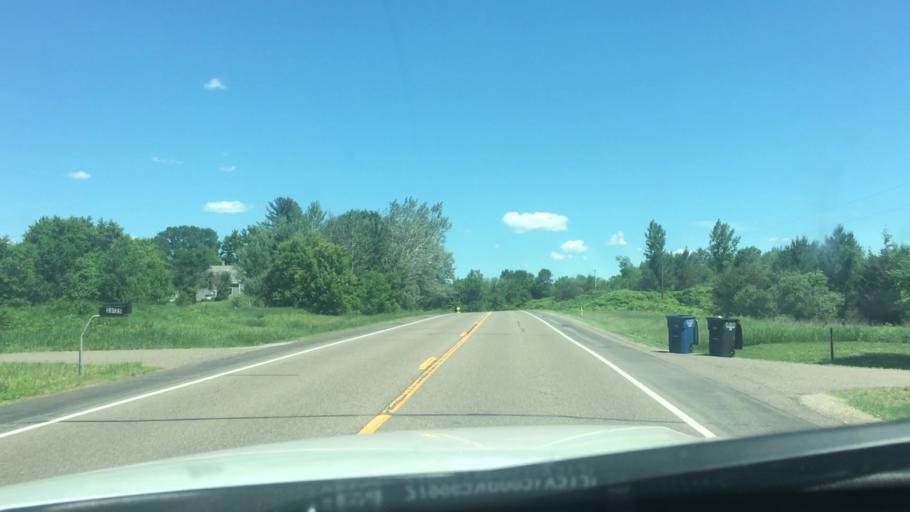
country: US
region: Wisconsin
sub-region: Polk County
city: Osceola
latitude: 45.3563
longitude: -92.7124
